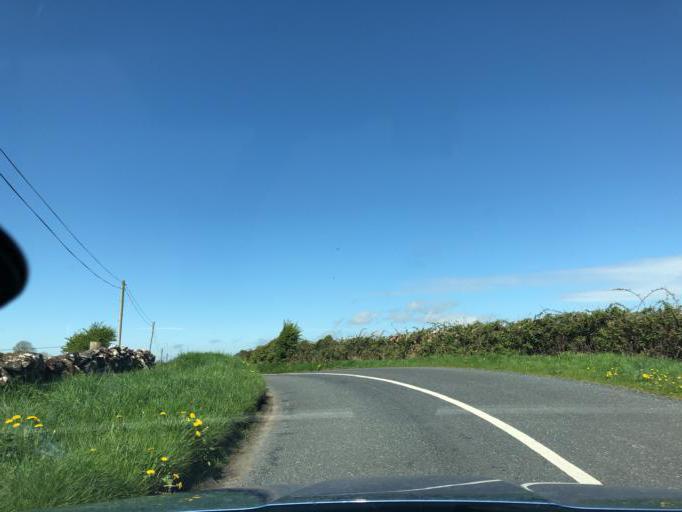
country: IE
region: Connaught
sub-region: County Galway
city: Loughrea
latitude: 53.1661
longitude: -8.4100
